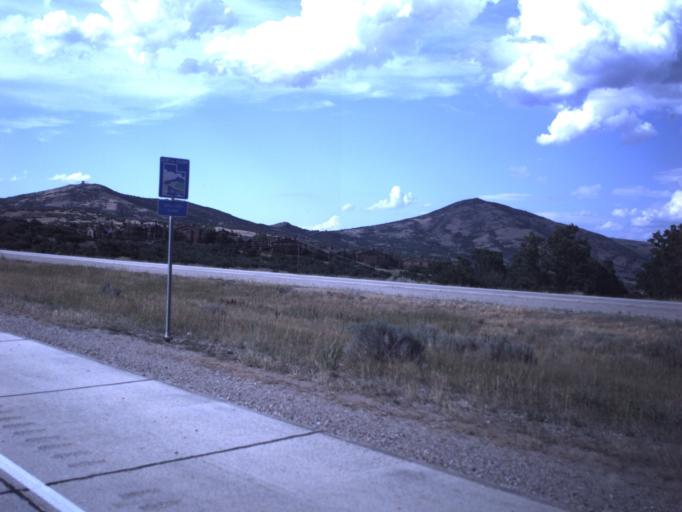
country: US
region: Utah
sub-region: Summit County
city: Park City
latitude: 40.6266
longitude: -111.4416
